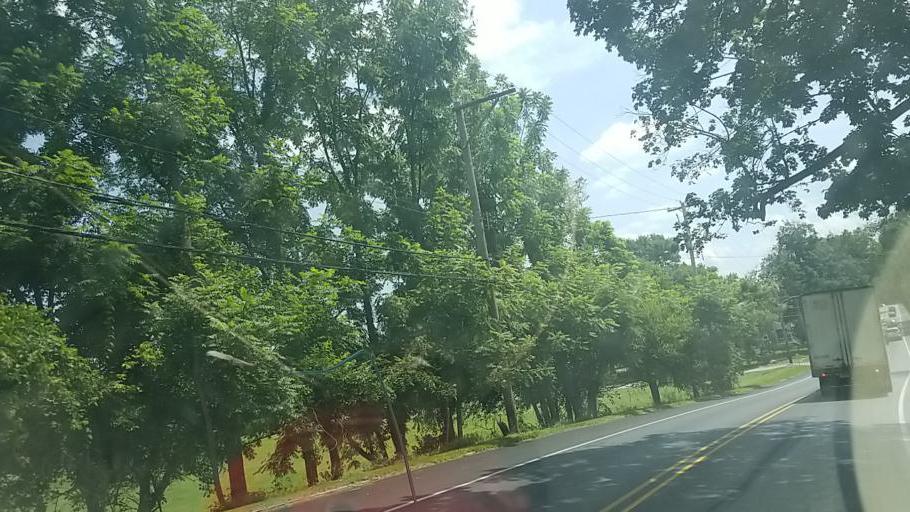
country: US
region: Pennsylvania
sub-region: Chester County
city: Avondale
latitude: 39.8304
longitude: -75.7865
